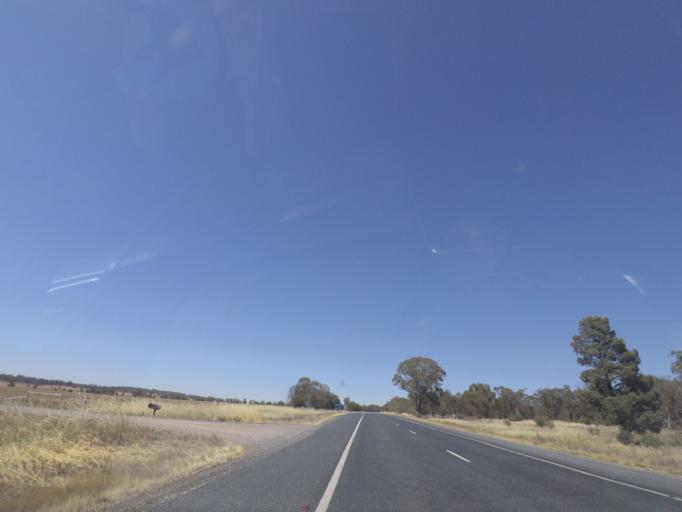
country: AU
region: New South Wales
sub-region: Narrandera
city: Narrandera
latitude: -34.4455
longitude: 146.8399
